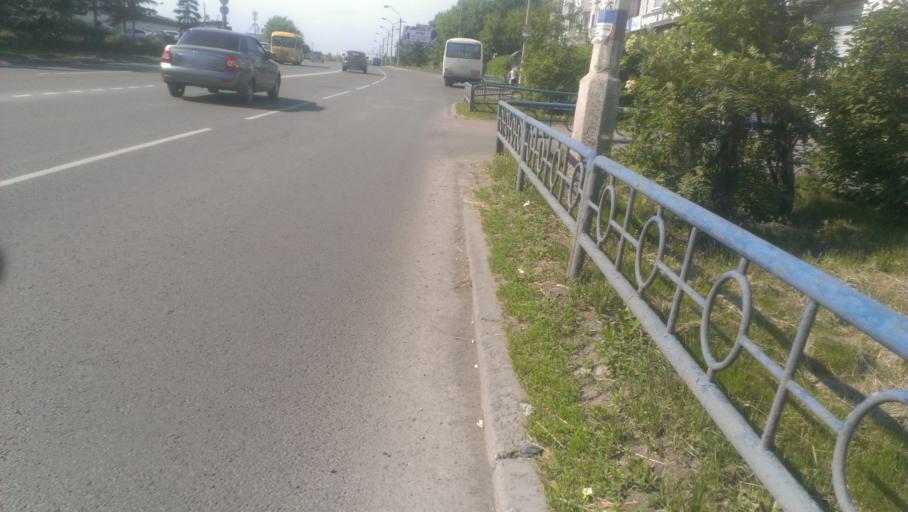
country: RU
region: Altai Krai
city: Novoaltaysk
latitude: 53.3935
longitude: 83.9336
